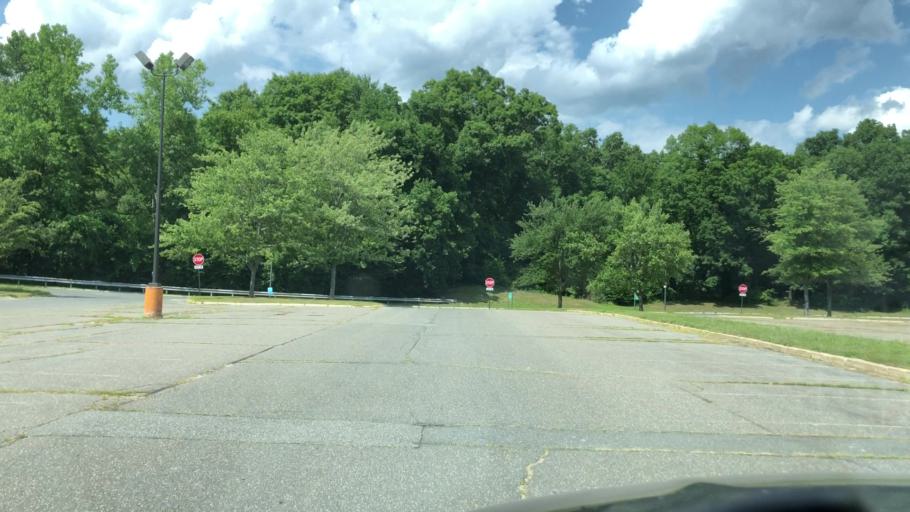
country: US
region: Massachusetts
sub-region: Hampden County
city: Holyoke
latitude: 42.1981
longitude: -72.6488
